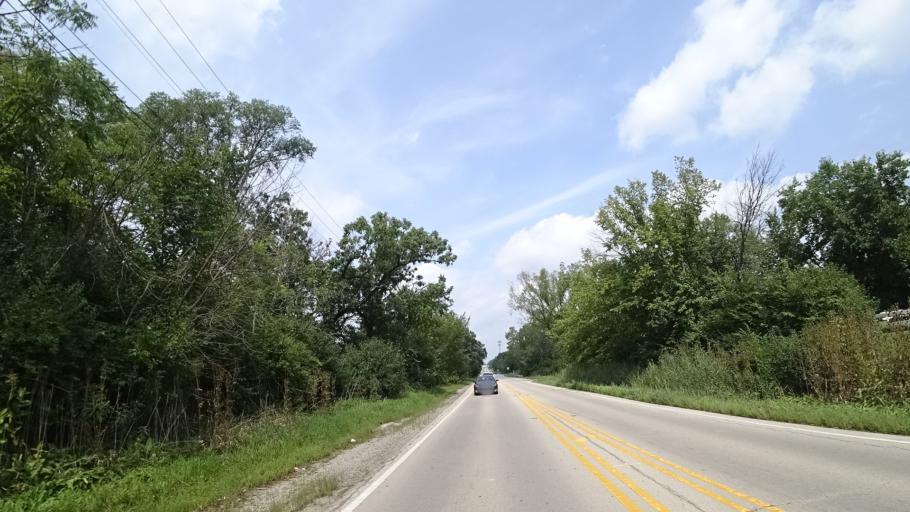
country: US
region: Illinois
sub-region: Cook County
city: Orland Park
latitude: 41.6261
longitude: -87.8923
